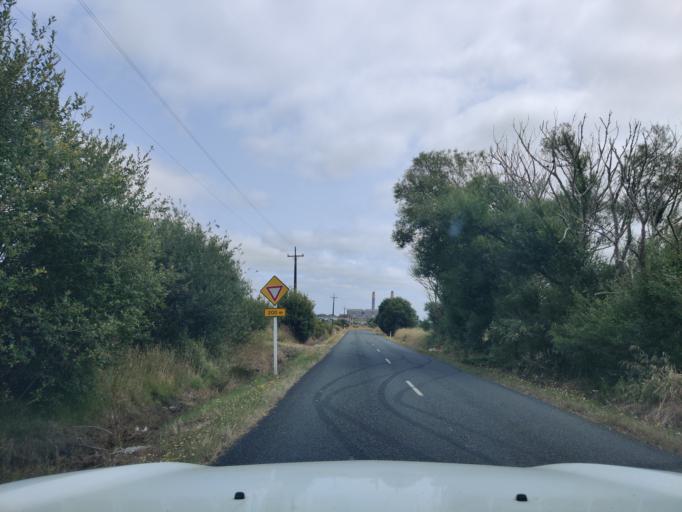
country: NZ
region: Waikato
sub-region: Waikato District
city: Te Kauwhata
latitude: -37.5298
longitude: 175.1649
